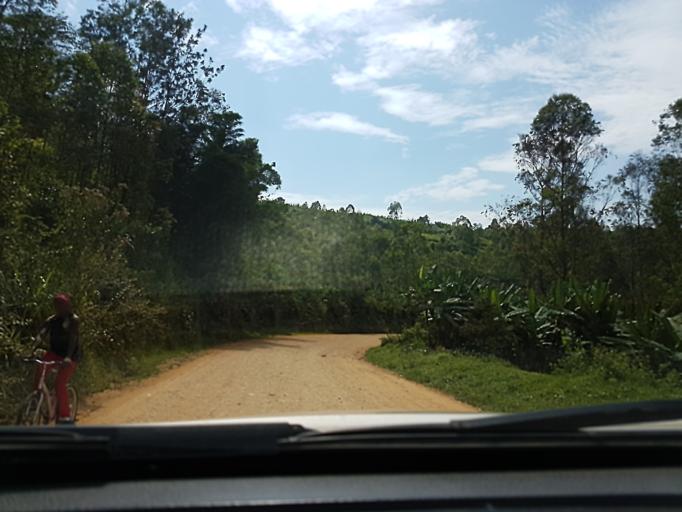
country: CD
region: South Kivu
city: Bukavu
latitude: -2.6346
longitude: 28.8758
